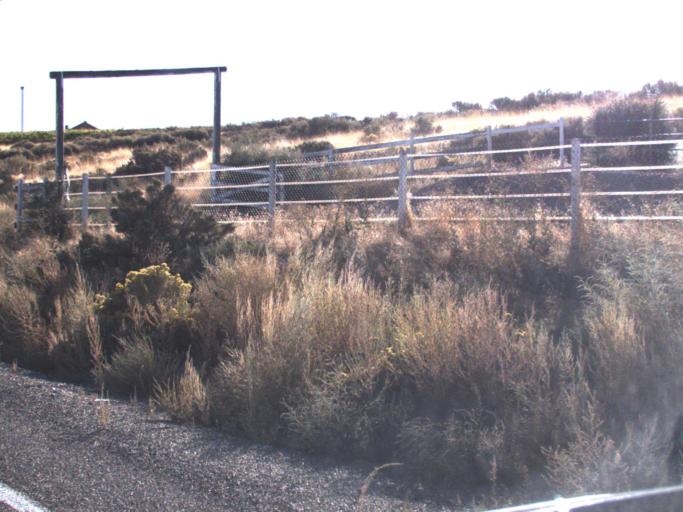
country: US
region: Washington
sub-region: Benton County
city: Benton City
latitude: 46.2601
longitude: -119.4652
